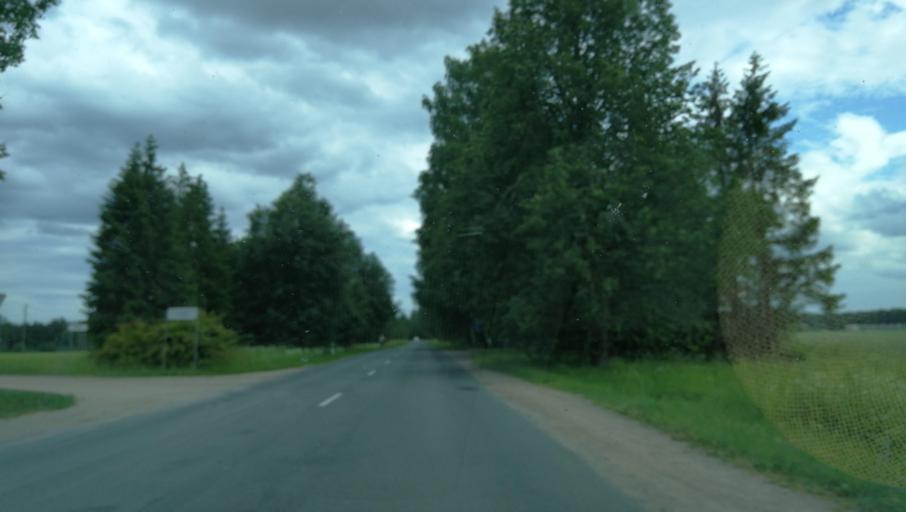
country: LV
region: Rujienas
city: Rujiena
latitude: 57.8783
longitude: 25.3596
